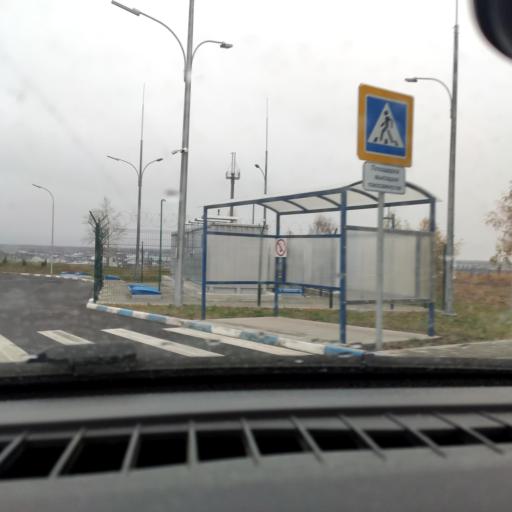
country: RU
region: Belgorod
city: Alekseyevka
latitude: 50.6447
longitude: 38.6773
